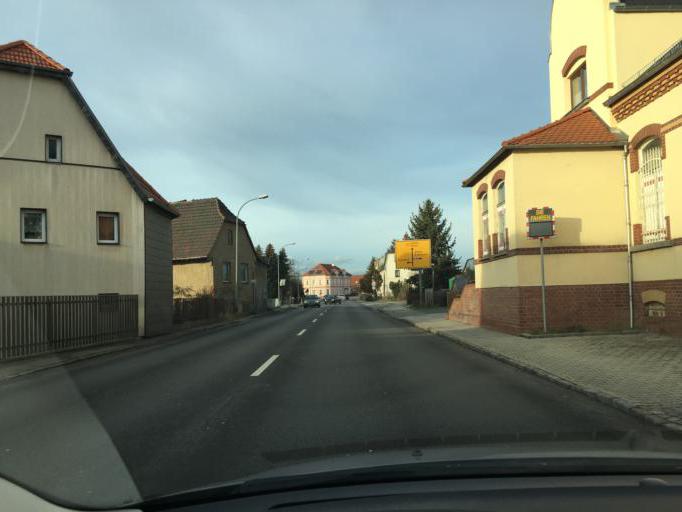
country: DE
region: Thuringia
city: Fockendorf
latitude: 51.0515
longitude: 12.4538
